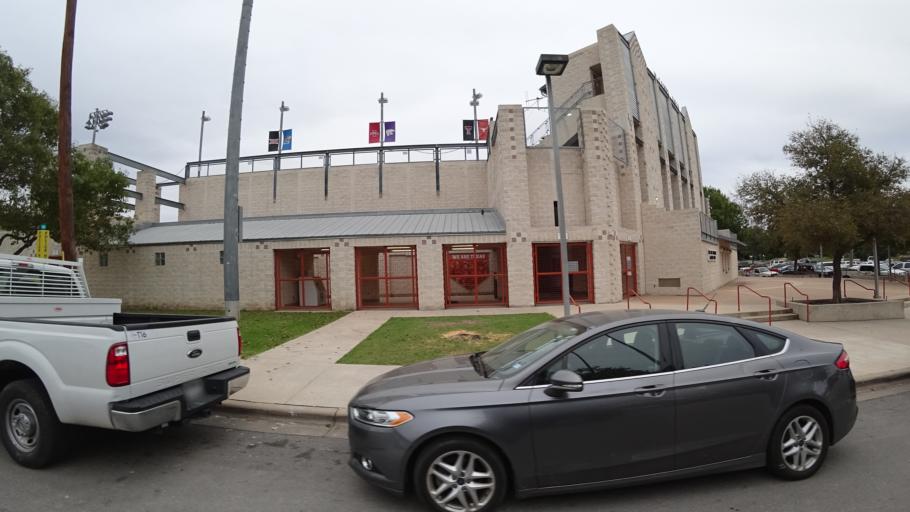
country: US
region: Texas
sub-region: Travis County
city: Austin
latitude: 30.2805
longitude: -97.7254
